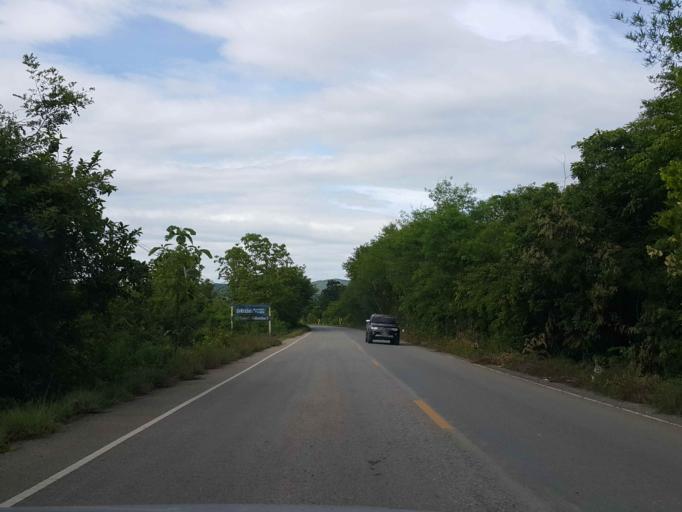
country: TH
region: Sukhothai
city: Thung Saliam
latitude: 17.2523
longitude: 99.5206
